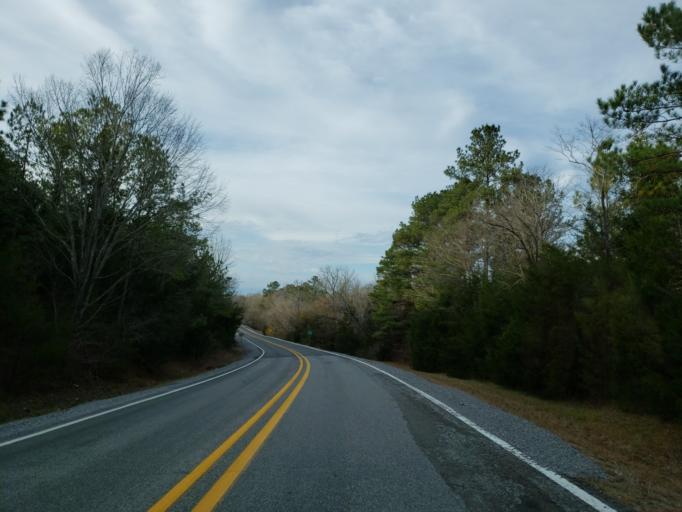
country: US
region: Mississippi
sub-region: Wayne County
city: Waynesboro
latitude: 31.8461
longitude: -88.6872
